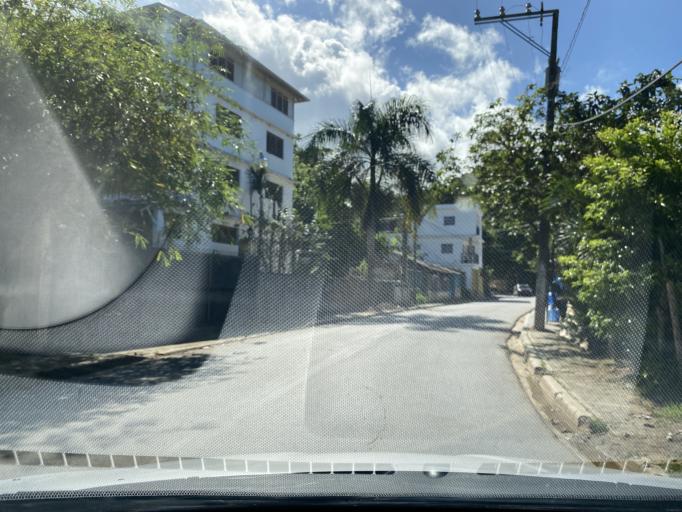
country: DO
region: Samana
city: Las Terrenas
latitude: 19.3182
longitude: -69.5296
